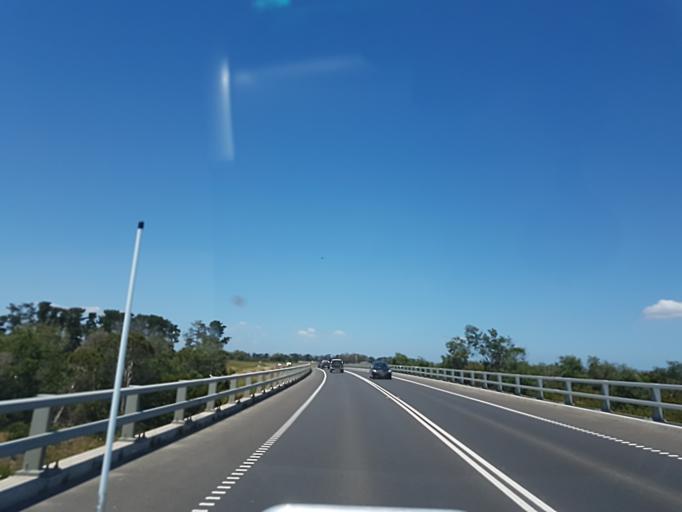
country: AU
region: Victoria
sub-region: Cardinia
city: Koo-Wee-Rup
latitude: -38.2012
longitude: 145.4718
